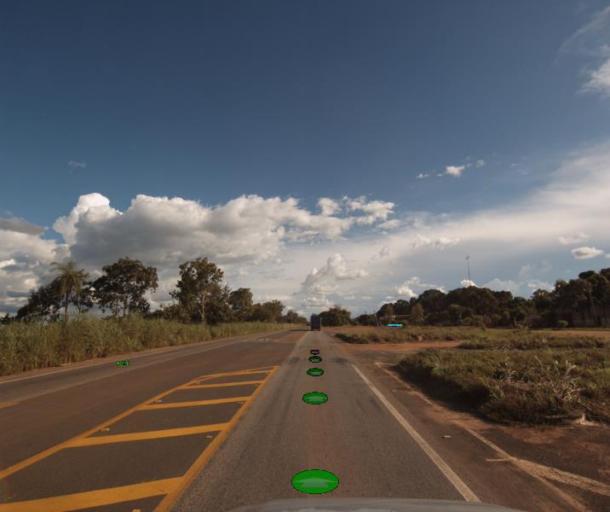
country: BR
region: Goias
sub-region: Porangatu
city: Porangatu
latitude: -13.1024
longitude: -49.1988
